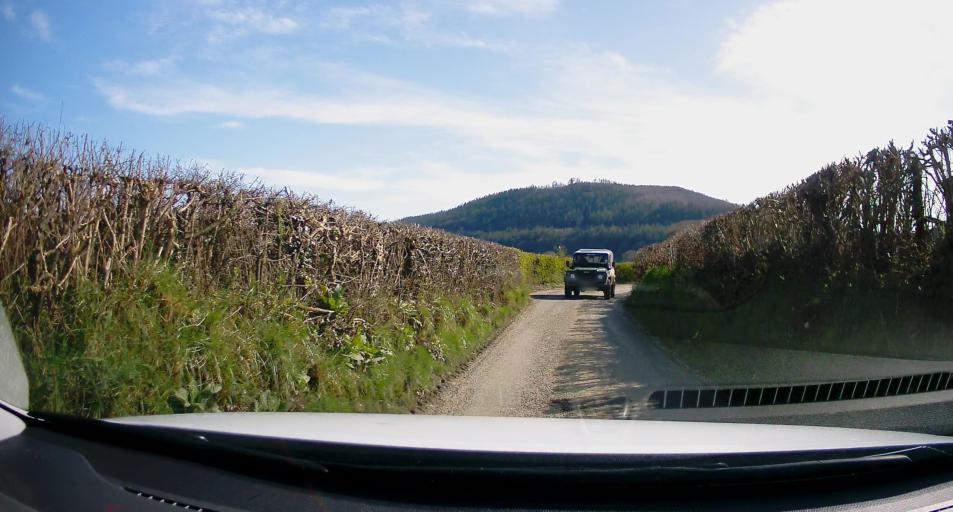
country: GB
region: Wales
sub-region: County of Ceredigion
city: Lledrod
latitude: 52.3308
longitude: -3.9549
